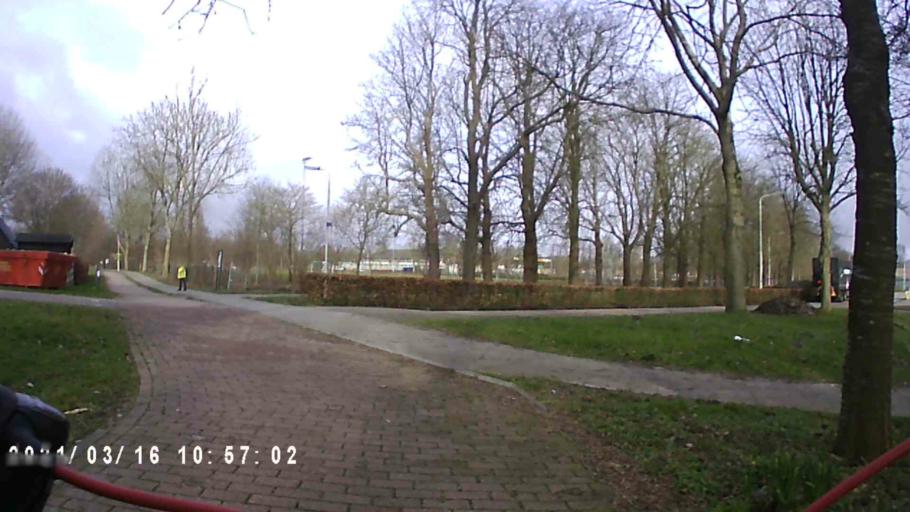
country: NL
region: Friesland
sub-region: Gemeente Dongeradeel
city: Dokkum
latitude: 53.3259
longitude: 6.0097
